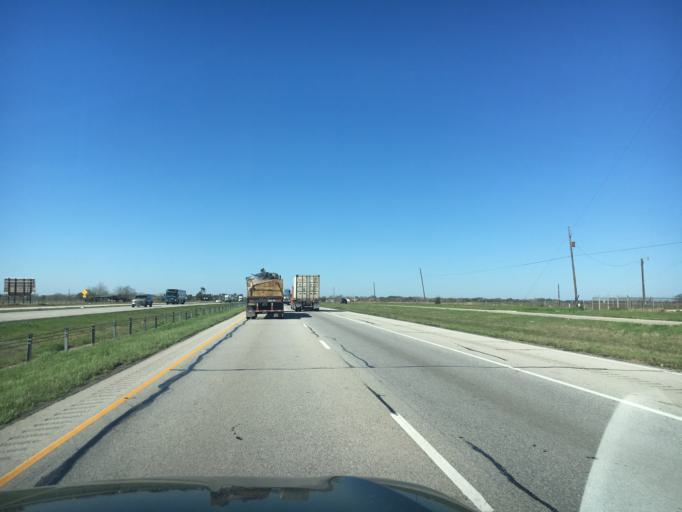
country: US
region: Texas
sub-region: Austin County
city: Sealy
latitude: 29.7506
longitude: -96.2859
